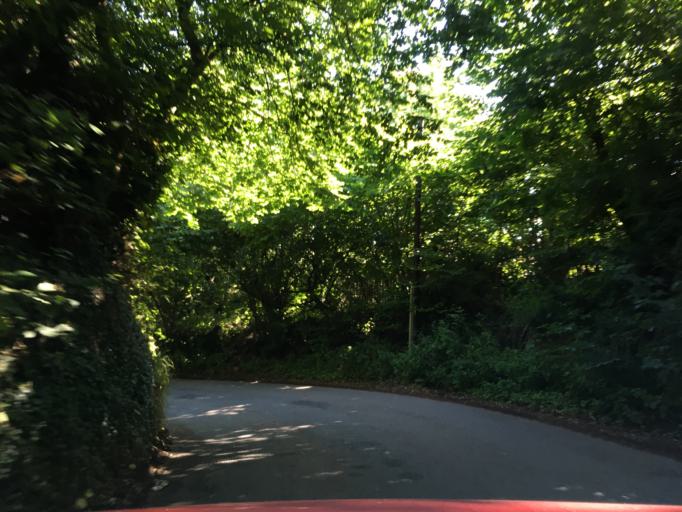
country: GB
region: England
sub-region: Herefordshire
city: Ross on Wye
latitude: 51.9277
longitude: -2.5792
